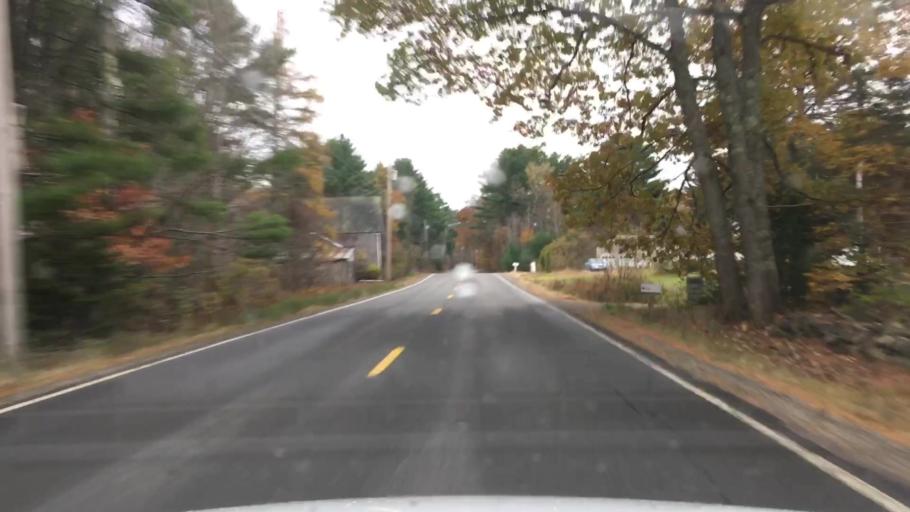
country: US
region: Maine
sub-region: Lincoln County
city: Jefferson
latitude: 44.1808
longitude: -69.4343
